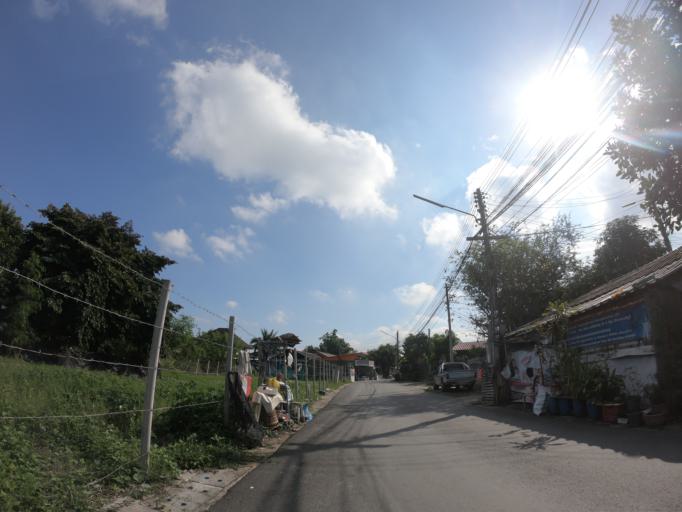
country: TH
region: Chiang Mai
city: Chiang Mai
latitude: 18.7870
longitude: 99.0362
